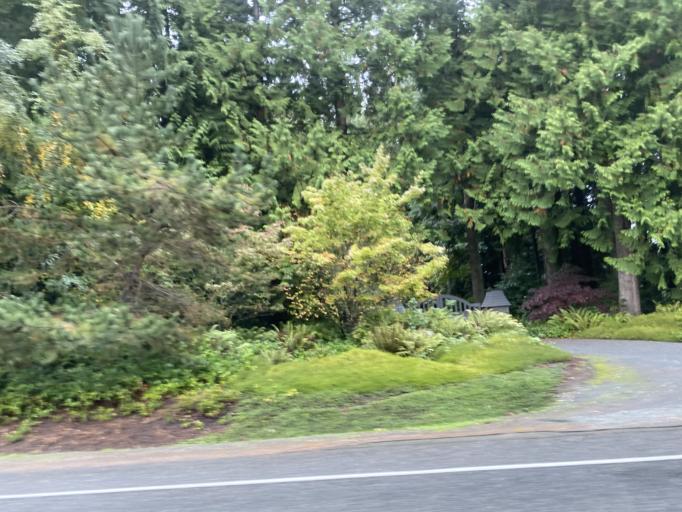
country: US
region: Washington
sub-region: Island County
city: Langley
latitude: 48.0402
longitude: -122.4258
